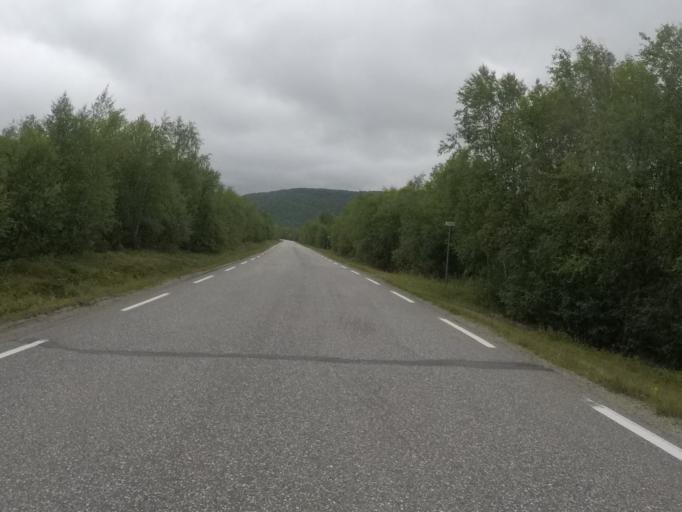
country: NO
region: Finnmark Fylke
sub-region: Karasjok
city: Karasjohka
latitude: 69.6433
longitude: 25.9513
